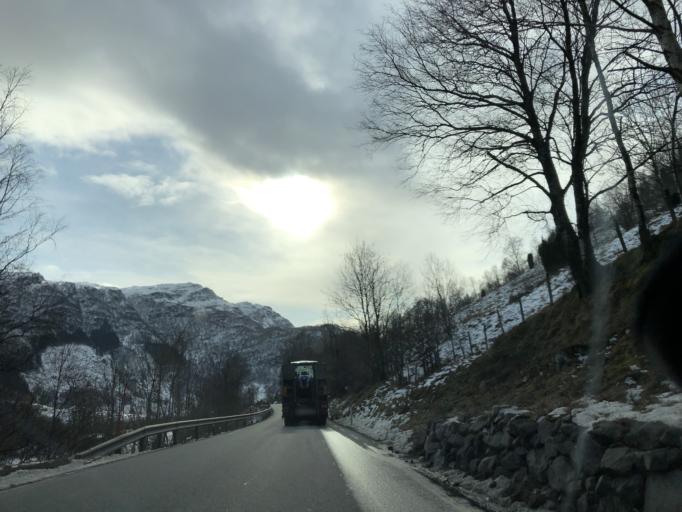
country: NO
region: Hordaland
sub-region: Etne
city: Etne
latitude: 59.7033
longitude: 6.0394
